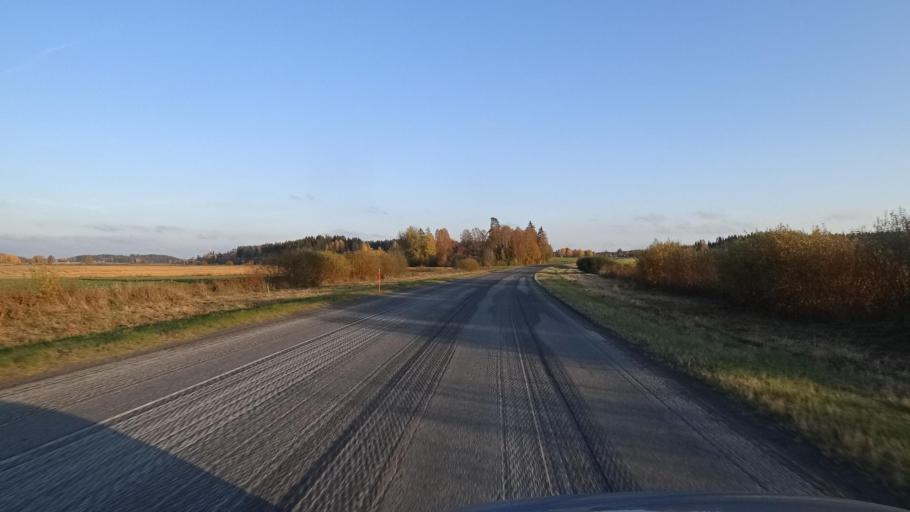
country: FI
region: Haeme
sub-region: Forssa
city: Ypaejae
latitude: 60.7848
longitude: 23.3030
